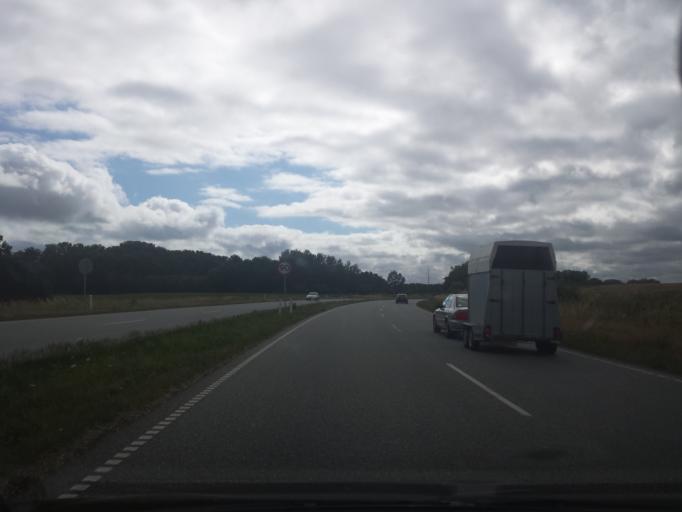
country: DK
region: South Denmark
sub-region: Sonderborg Kommune
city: Augustenborg
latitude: 54.9463
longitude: 9.8936
